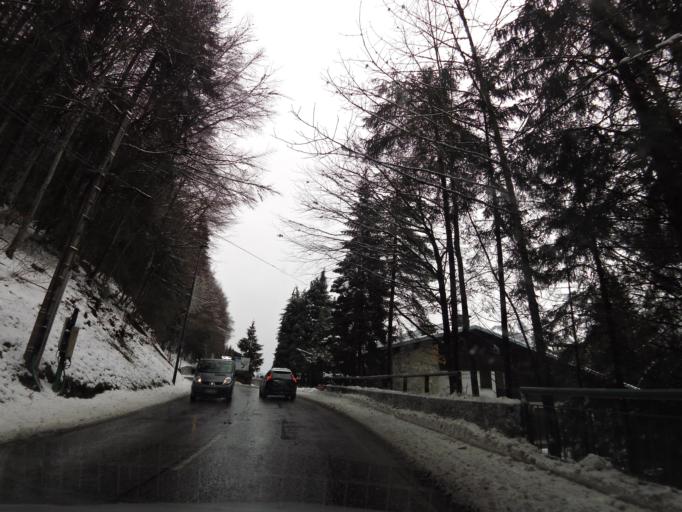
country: FR
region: Rhone-Alpes
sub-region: Departement de la Haute-Savoie
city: Morzine
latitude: 46.1863
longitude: 6.6935
